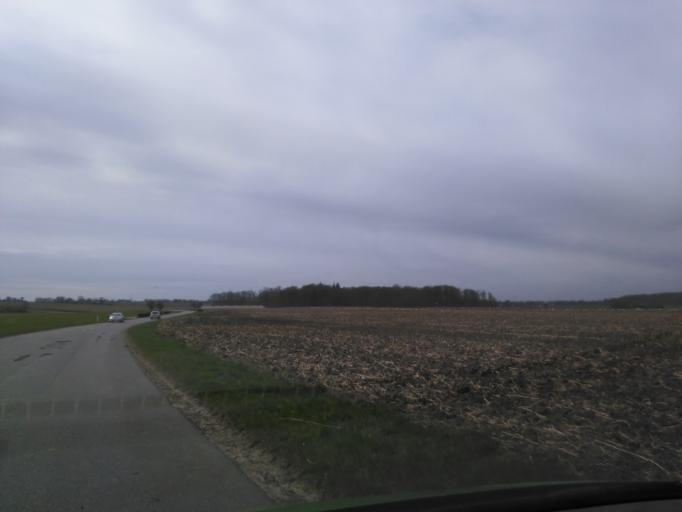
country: DK
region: Central Jutland
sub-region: Arhus Kommune
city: Malling
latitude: 55.9683
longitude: 10.2343
